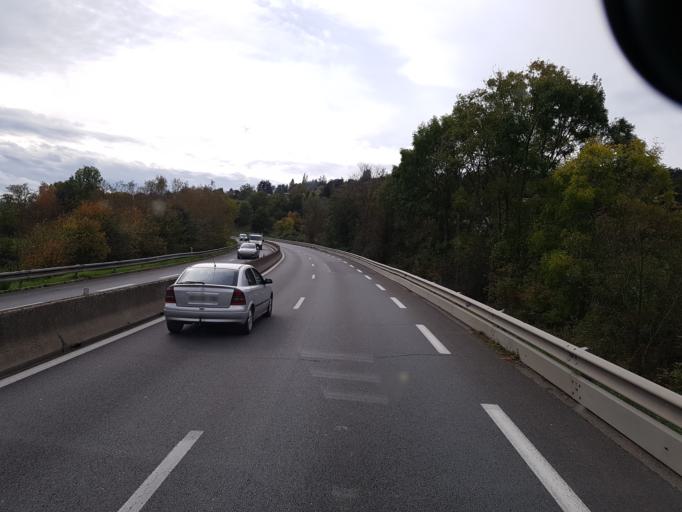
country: FR
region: Rhone-Alpes
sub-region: Departement de la Loire
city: Saint-Genest-Lerpt
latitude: 45.4639
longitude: 4.3366
